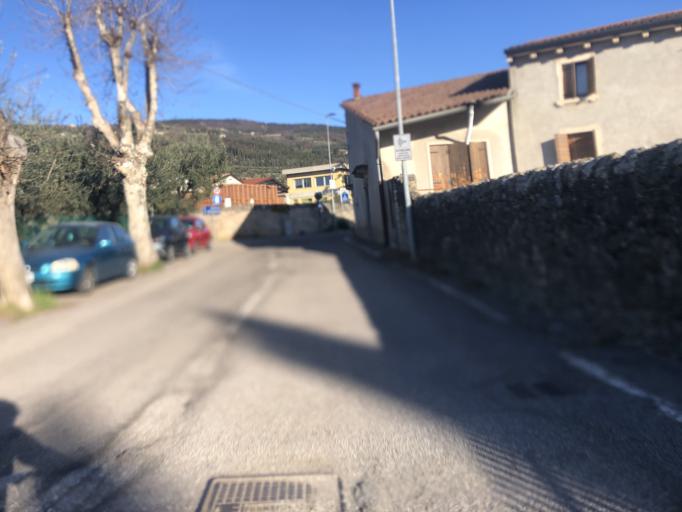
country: IT
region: Veneto
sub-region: Provincia di Verona
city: Fumane
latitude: 45.5355
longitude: 10.8789
